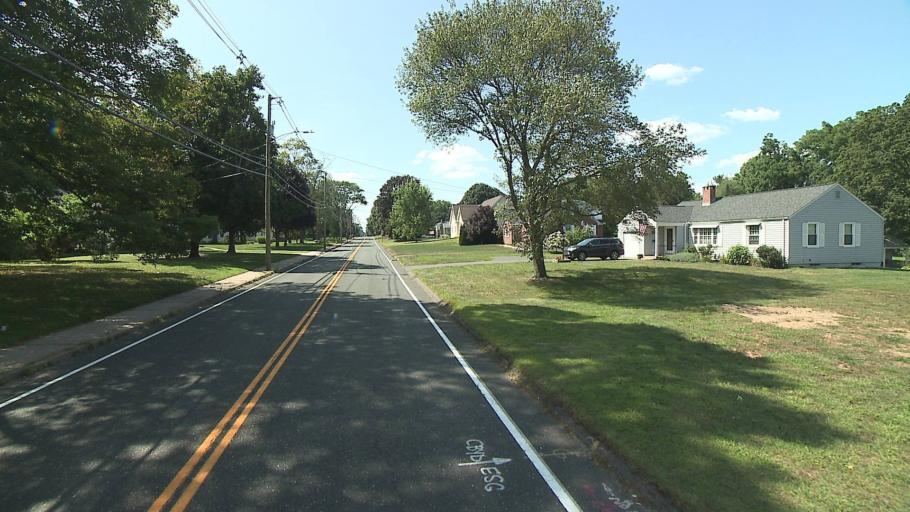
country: US
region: Connecticut
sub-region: Hartford County
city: Windsor Locks
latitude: 41.9260
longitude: -72.6347
